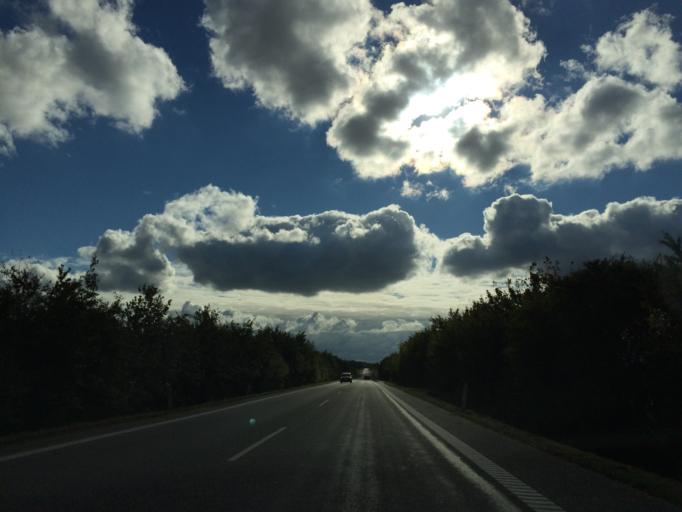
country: DK
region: Central Jutland
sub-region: Skanderborg Kommune
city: Ry
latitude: 56.1320
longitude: 9.7949
